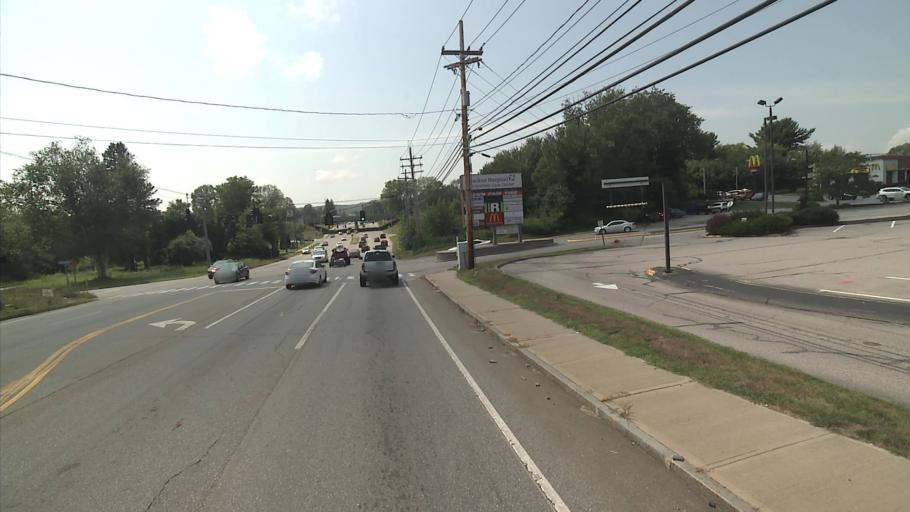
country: US
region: Connecticut
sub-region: New London County
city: Norwich
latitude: 41.5111
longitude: -72.1138
